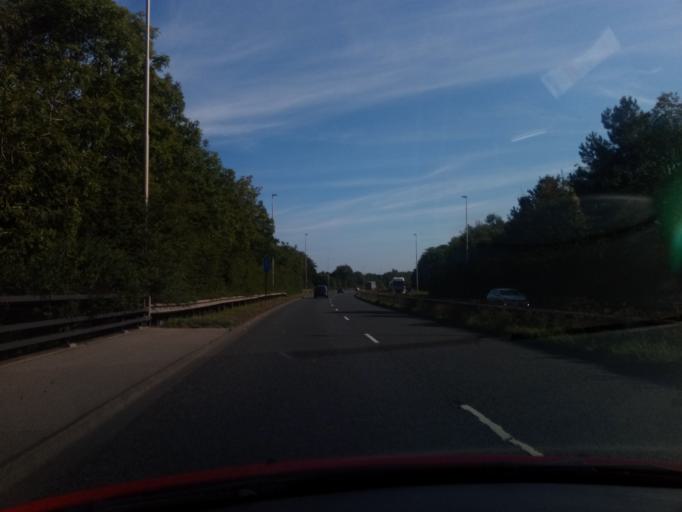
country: GB
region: England
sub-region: Sunderland
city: Washington
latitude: 54.9063
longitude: -1.4825
